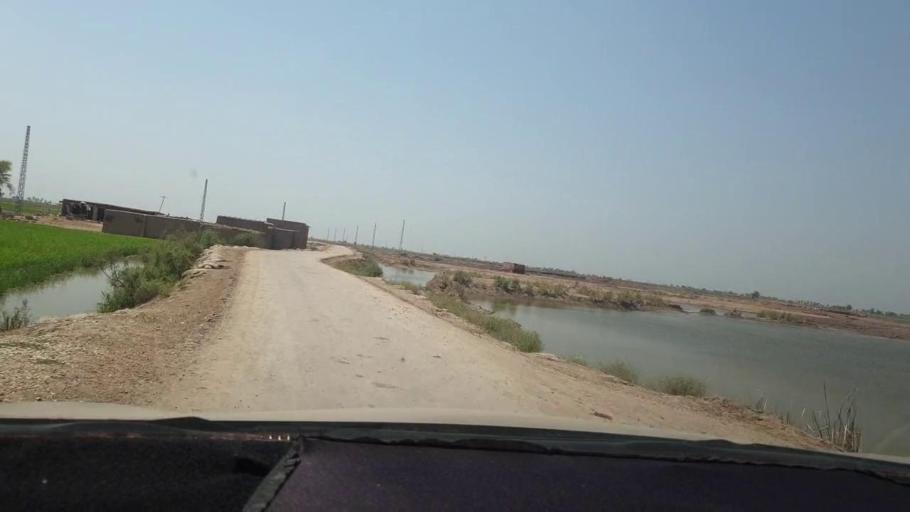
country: PK
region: Sindh
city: Shahdadkot
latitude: 27.8340
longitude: 67.8874
